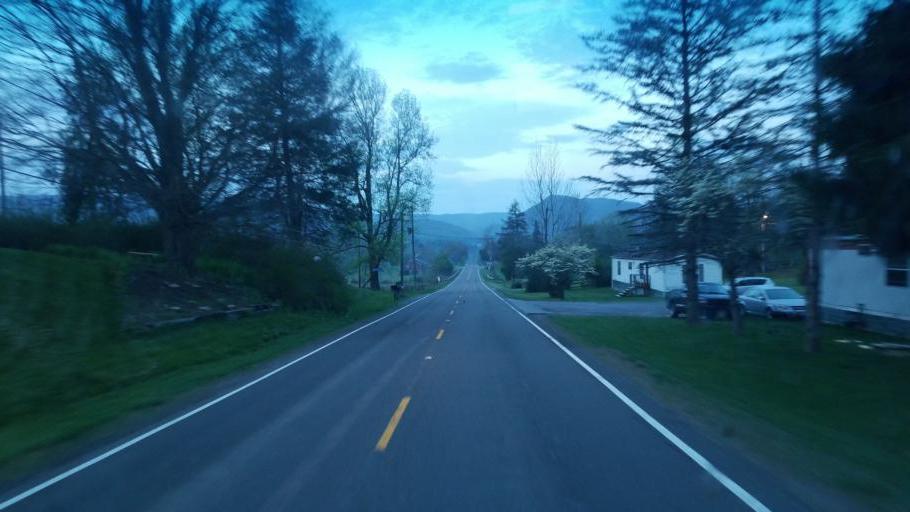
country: US
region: Virginia
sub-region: Smyth County
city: Atkins
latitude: 36.7858
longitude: -81.4042
